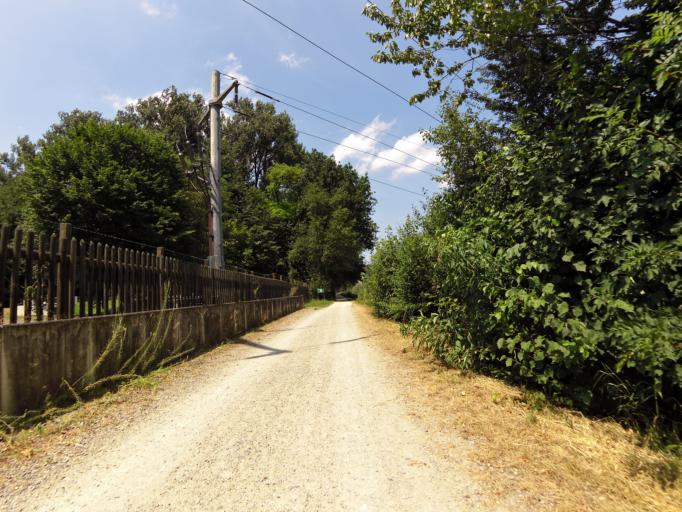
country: CH
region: Zurich
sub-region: Bezirk Dietikon
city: Geroldswil
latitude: 47.4122
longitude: 8.4081
